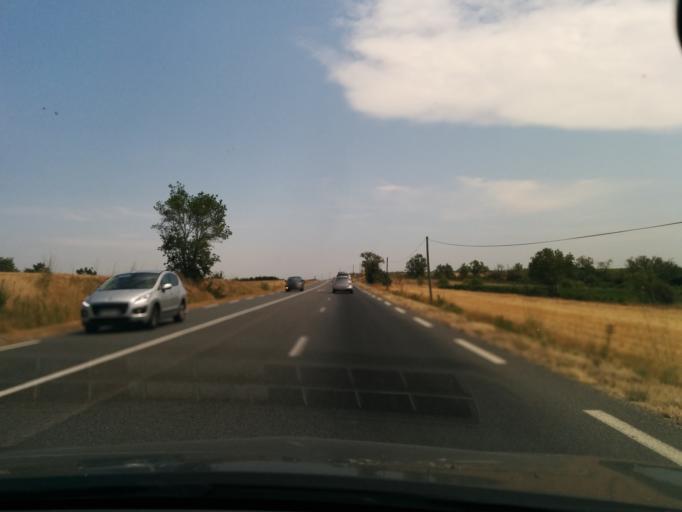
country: FR
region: Languedoc-Roussillon
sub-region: Departement de l'Aude
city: Pezens
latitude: 43.2516
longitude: 2.2775
